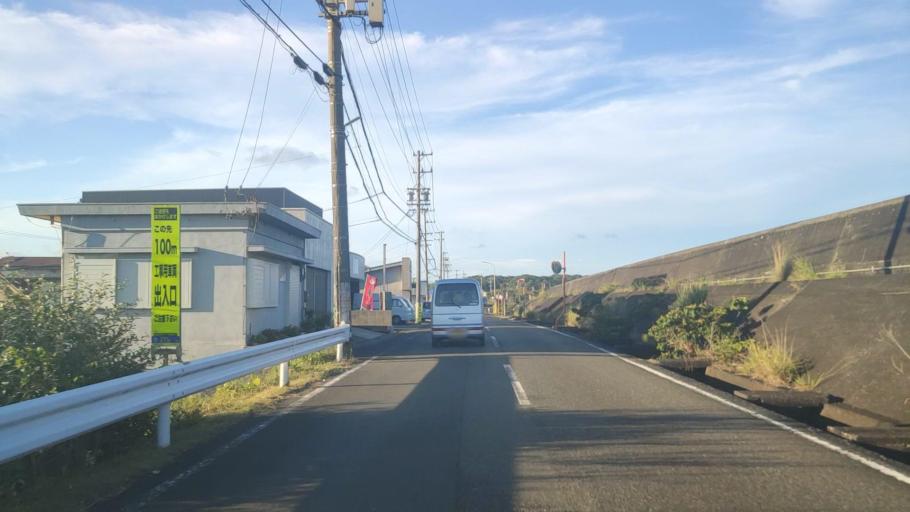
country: JP
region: Mie
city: Toba
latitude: 34.2587
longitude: 136.8488
